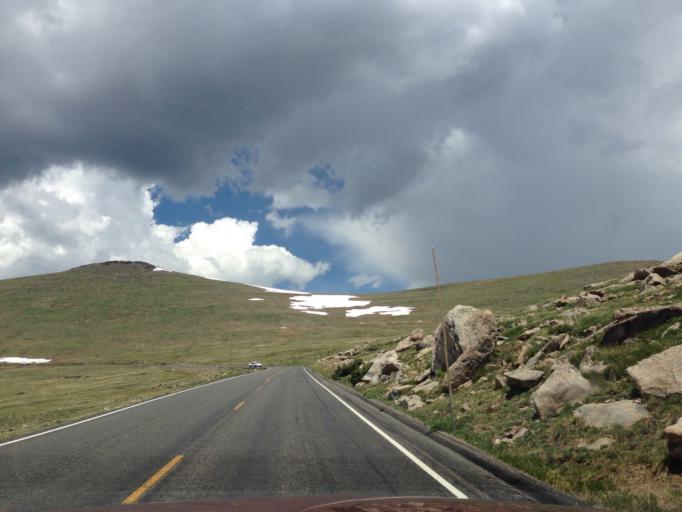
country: US
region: Colorado
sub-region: Larimer County
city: Estes Park
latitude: 40.3996
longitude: -105.7103
